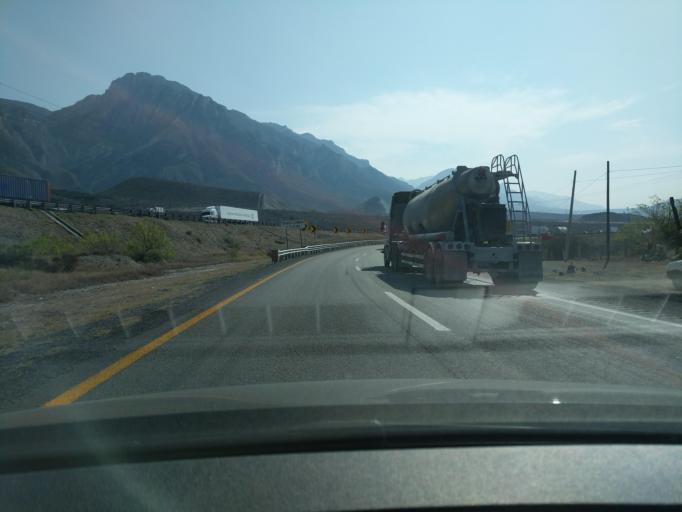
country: MX
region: Nuevo Leon
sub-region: Garcia
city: Las Torres de Guadalupe
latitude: 25.6802
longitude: -100.6658
